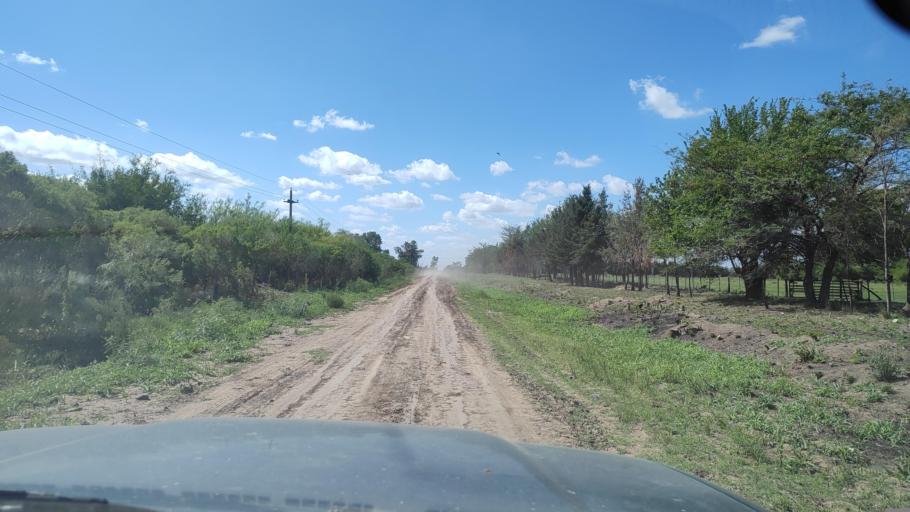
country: AR
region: Buenos Aires
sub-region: Partido de Lujan
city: Lujan
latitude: -34.5328
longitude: -59.1493
